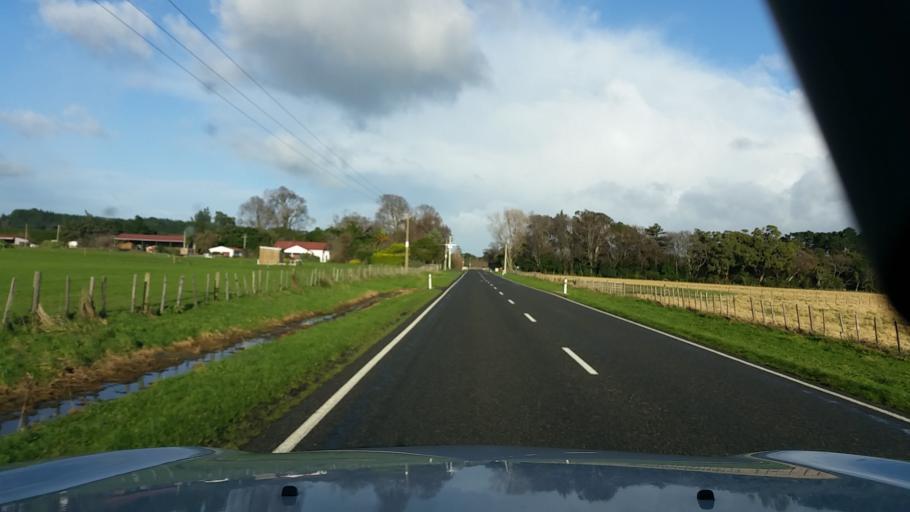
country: NZ
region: Wellington
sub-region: South Wairarapa District
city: Waipawa
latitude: -41.3157
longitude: 175.2599
